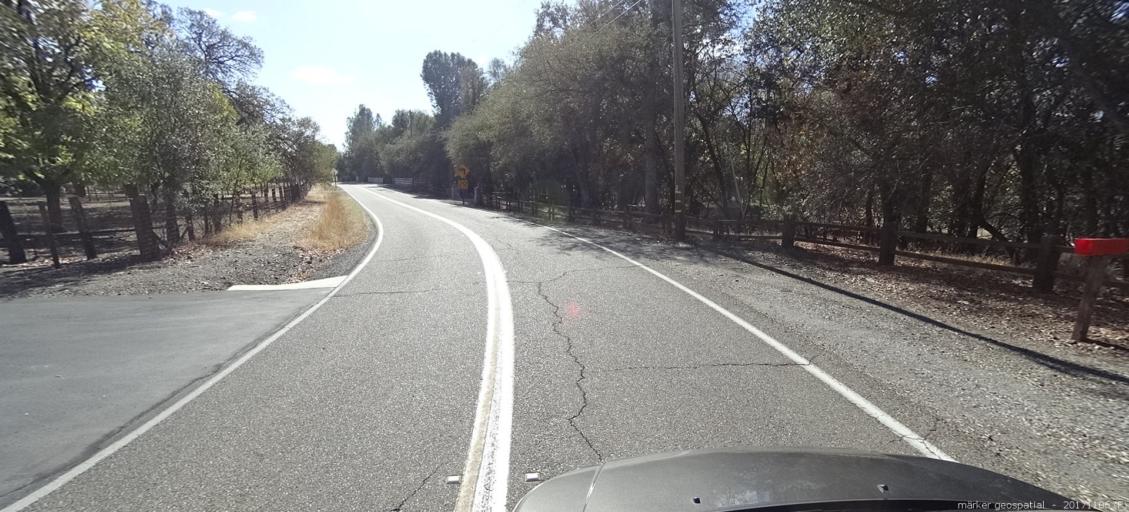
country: US
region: California
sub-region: Shasta County
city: Palo Cedro
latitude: 40.5834
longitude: -122.2240
